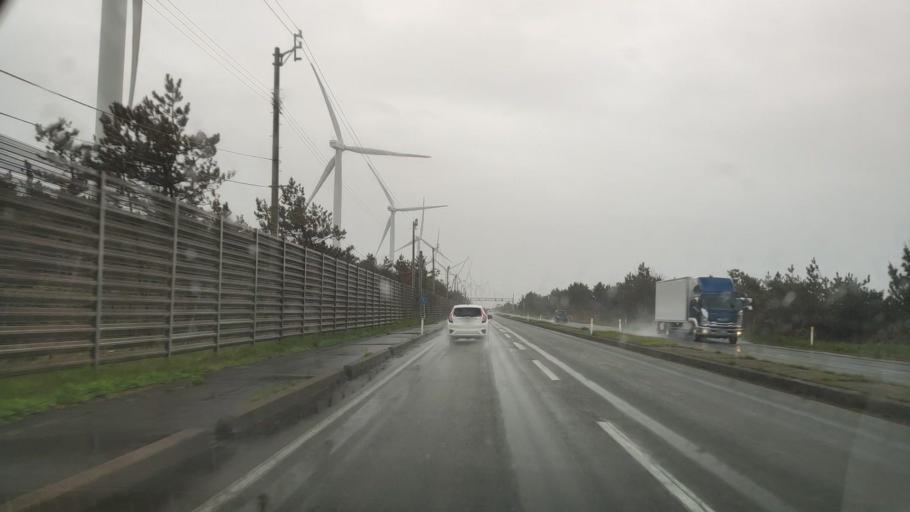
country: JP
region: Akita
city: Tenno
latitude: 39.8269
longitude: 140.0228
